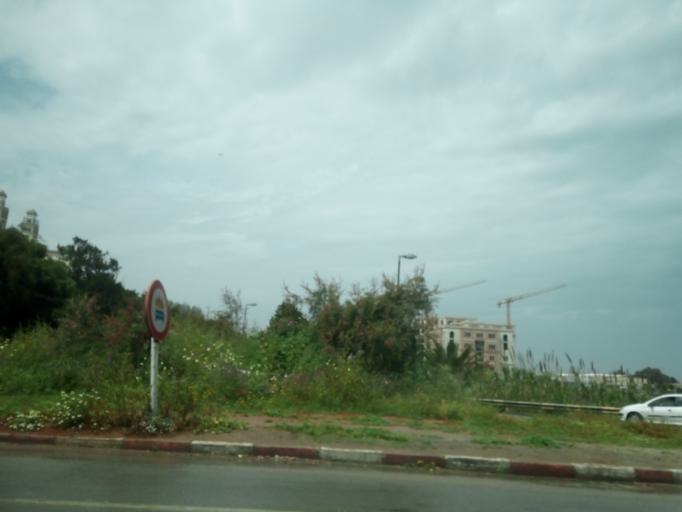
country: DZ
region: Alger
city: Bab Ezzouar
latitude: 36.7336
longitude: 3.1197
